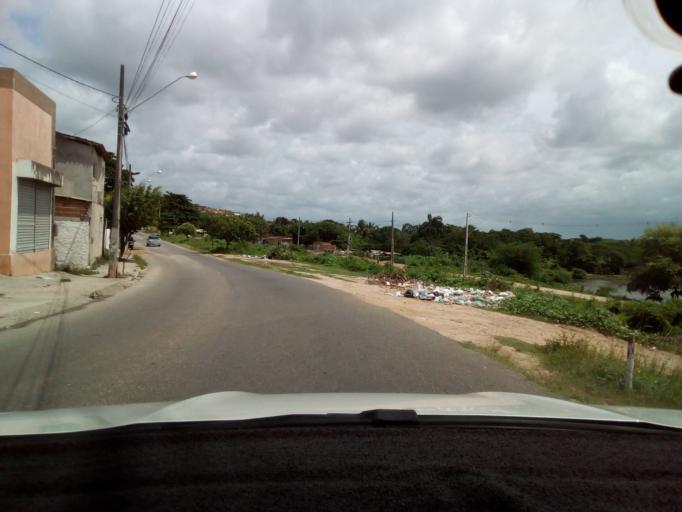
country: BR
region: Paraiba
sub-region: Joao Pessoa
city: Joao Pessoa
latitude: -7.1057
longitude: -34.8780
